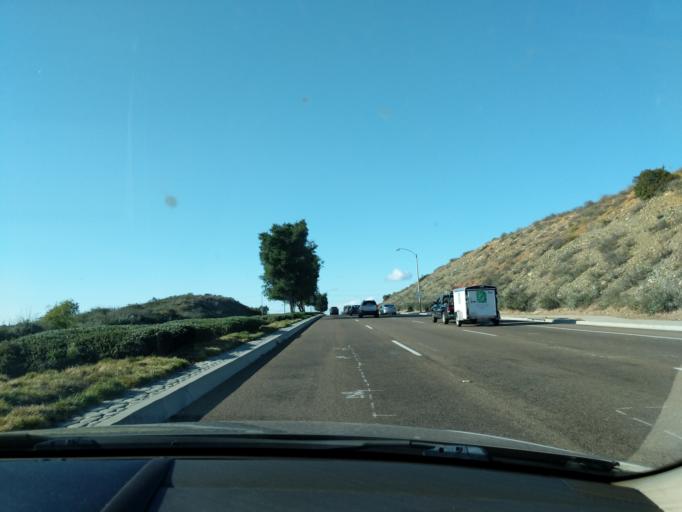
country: US
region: California
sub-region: San Diego County
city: Lake San Marcos
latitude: 33.0901
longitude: -117.2251
